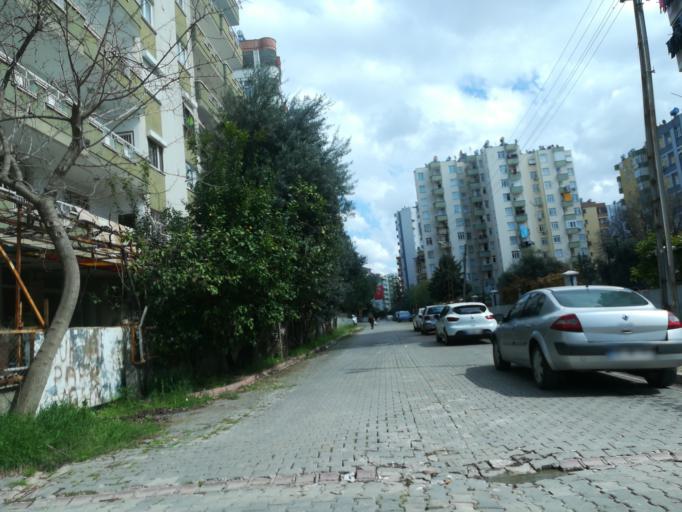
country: TR
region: Adana
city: Adana
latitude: 37.0316
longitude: 35.2969
